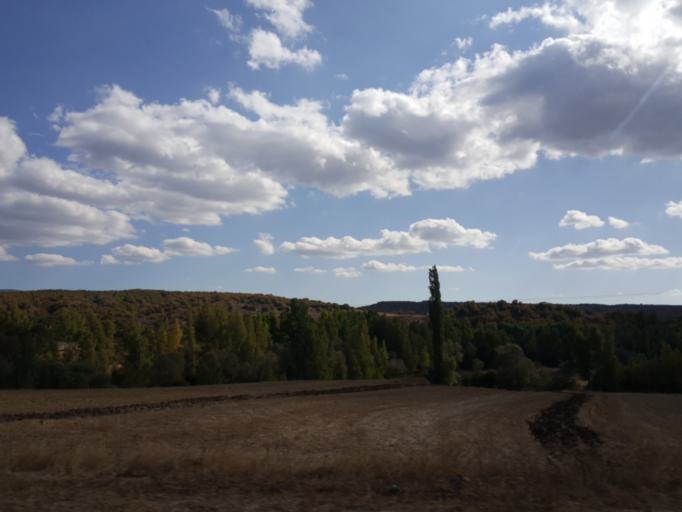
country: TR
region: Tokat
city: Sulusaray
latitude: 39.9736
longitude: 36.0415
